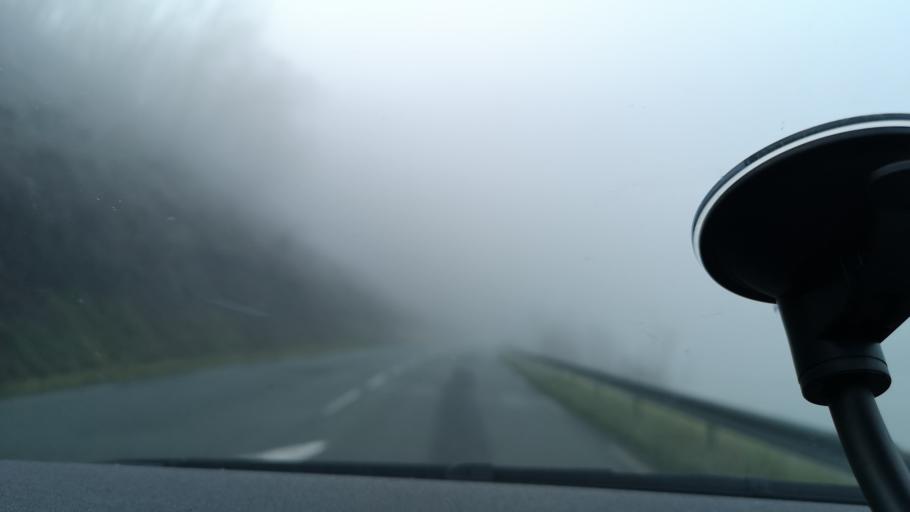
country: FR
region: Franche-Comte
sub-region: Departement du Doubs
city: Clerval
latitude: 47.4151
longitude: 6.5592
